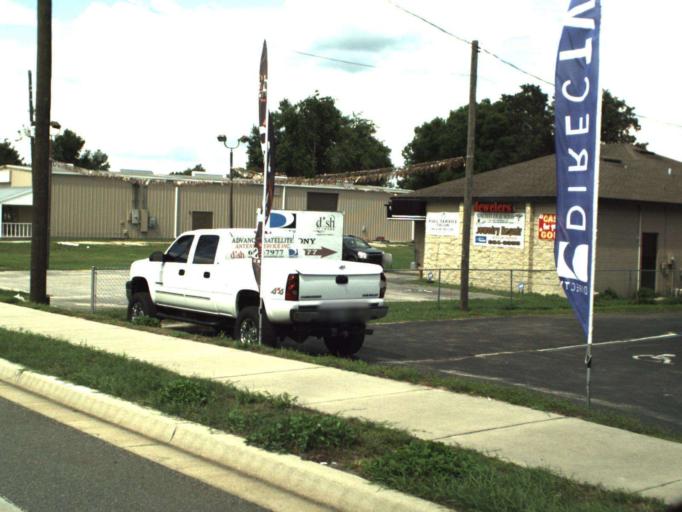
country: US
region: Florida
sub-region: Marion County
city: Silver Springs Shores
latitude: 29.1606
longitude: -82.0535
